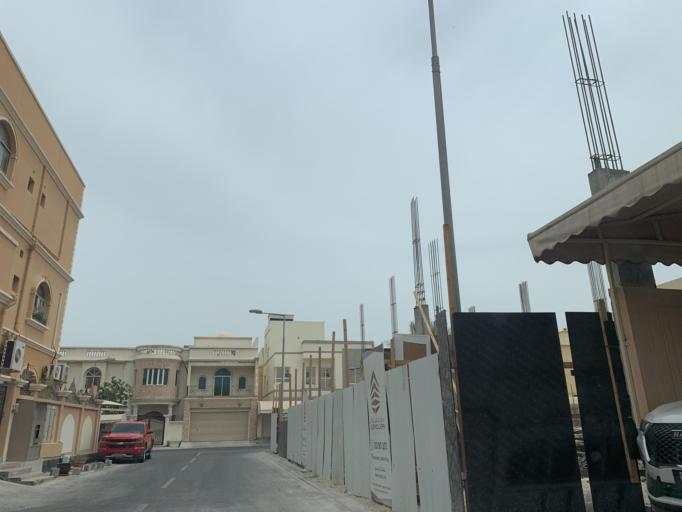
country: BH
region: Northern
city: Ar Rifa'
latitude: 26.1363
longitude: 50.5618
